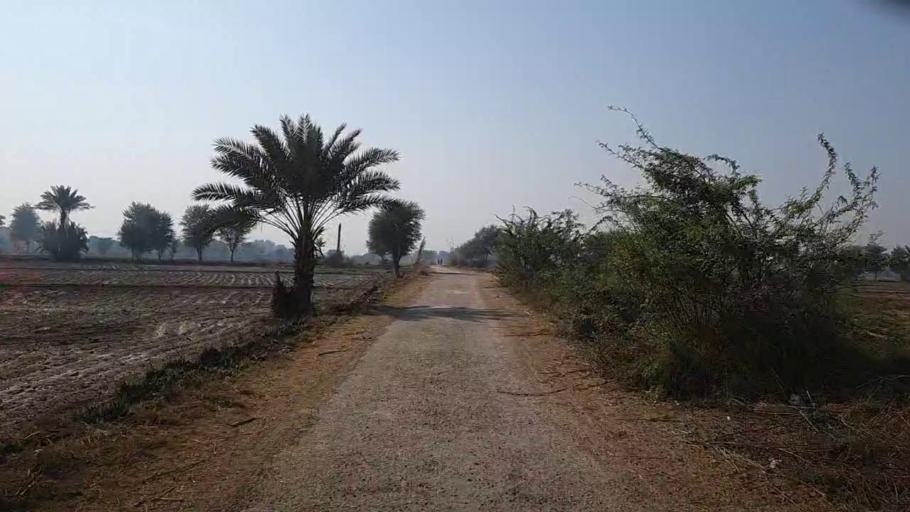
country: PK
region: Sindh
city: Bozdar
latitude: 27.2474
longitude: 68.6073
